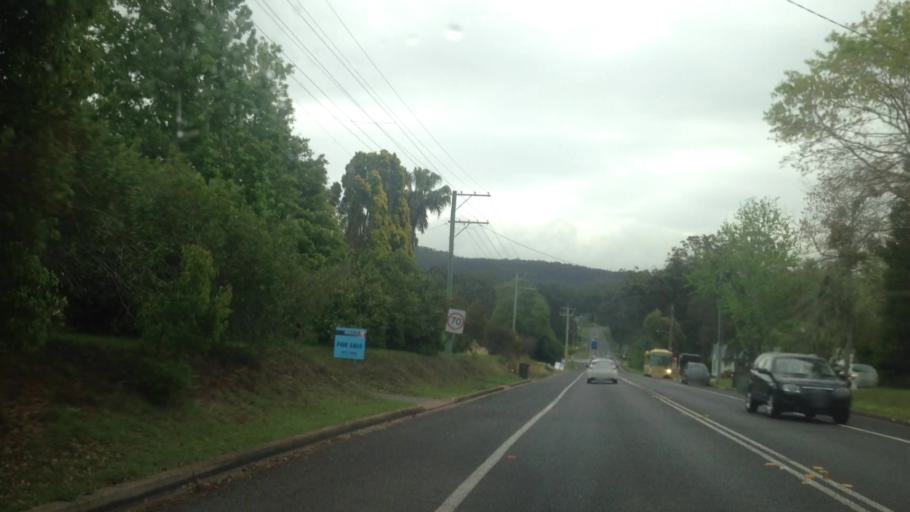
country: AU
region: New South Wales
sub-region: Lake Macquarie Shire
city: Cooranbong
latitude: -33.0934
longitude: 151.4640
